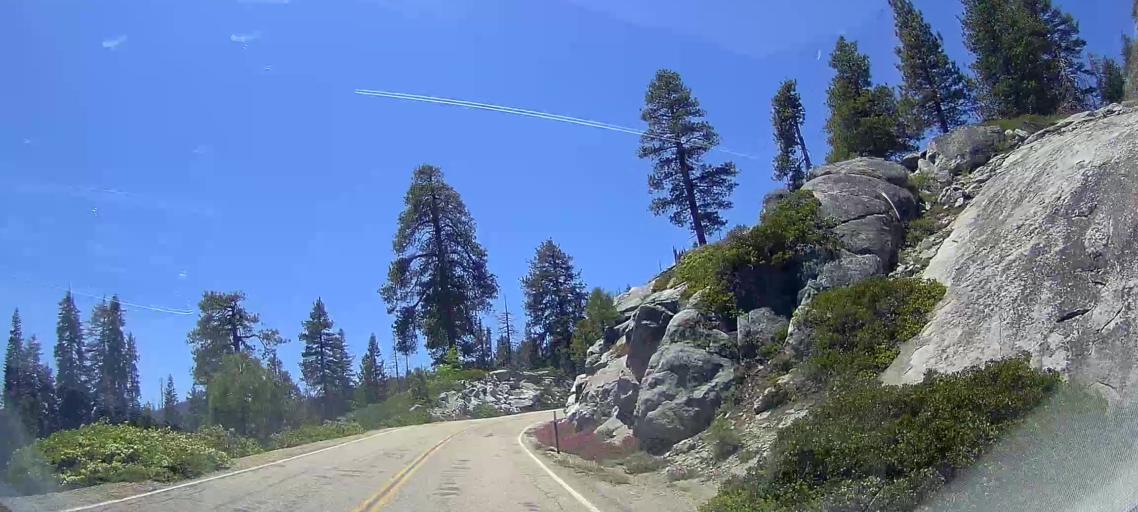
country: US
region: California
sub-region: Tulare County
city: Three Rivers
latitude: 36.6993
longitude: -118.8722
